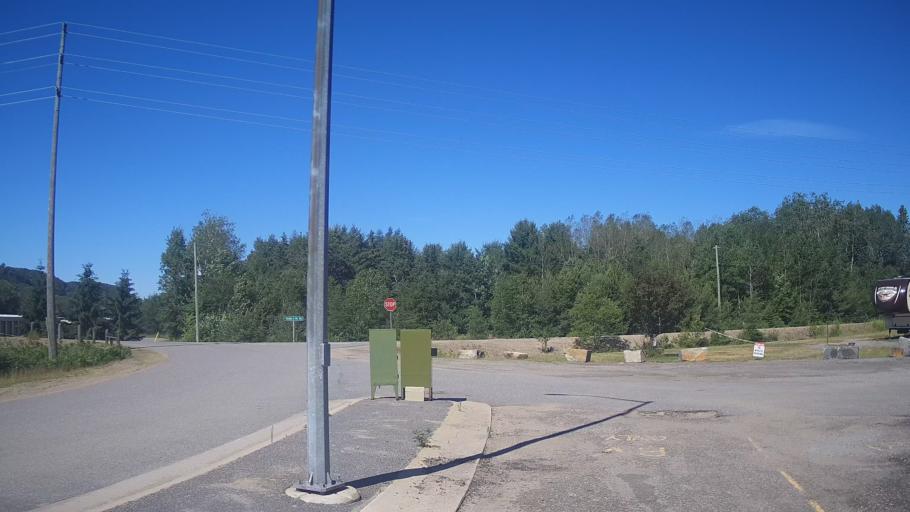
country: CA
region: Ontario
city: Huntsville
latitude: 45.3743
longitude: -79.2141
